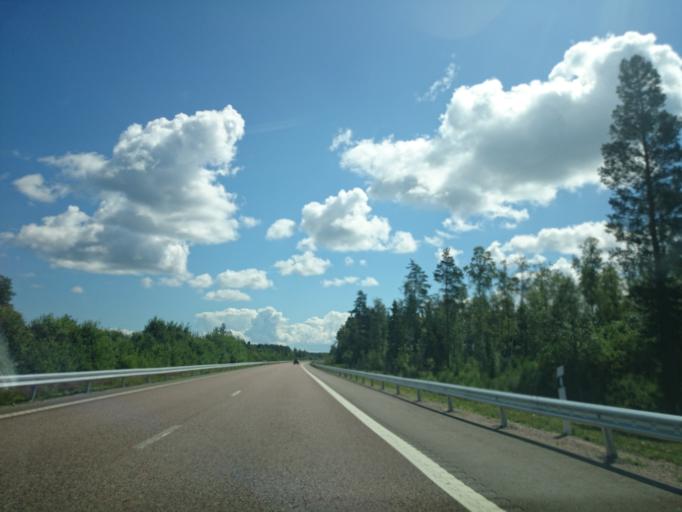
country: SE
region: Gaevleborg
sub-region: Gavle Kommun
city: Gavle
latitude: 60.5830
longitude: 17.2075
